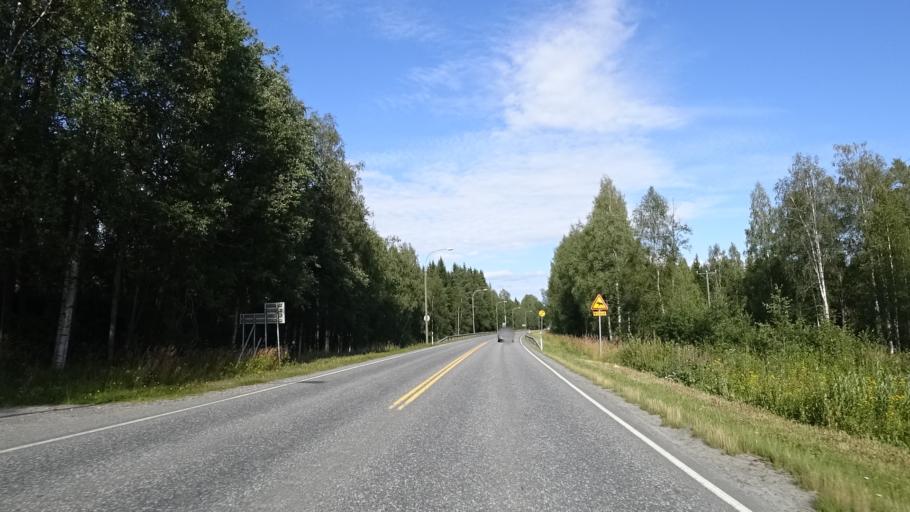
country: FI
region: North Karelia
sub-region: Joensuu
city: Eno
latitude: 62.7938
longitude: 30.0885
